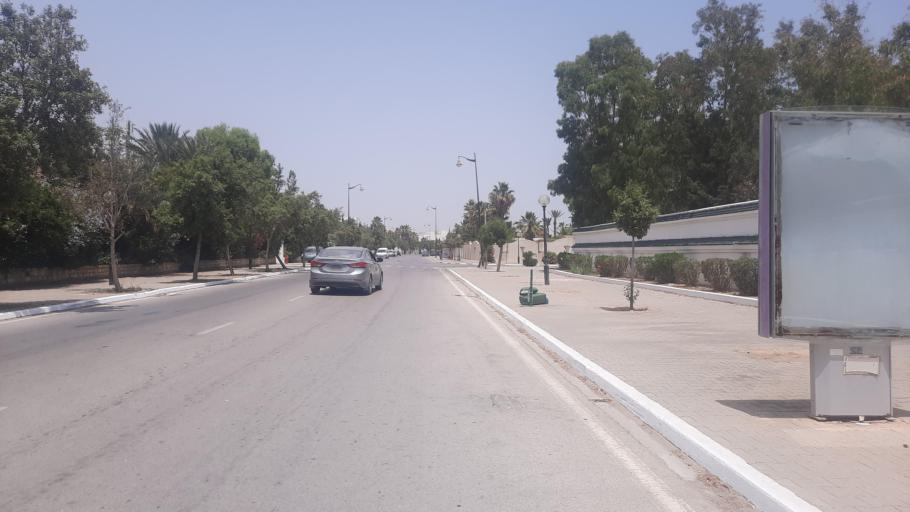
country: TN
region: Nabul
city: Al Hammamat
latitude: 36.3579
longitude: 10.5284
